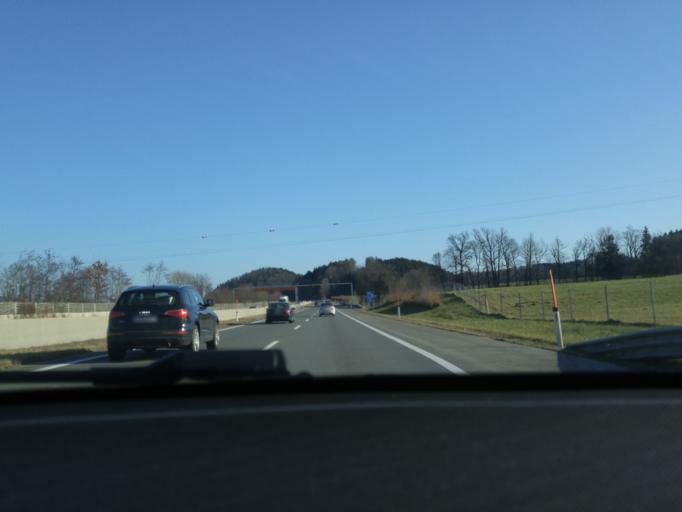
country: AT
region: Salzburg
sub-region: Politischer Bezirk Salzburg-Umgebung
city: Plainfeld
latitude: 47.8517
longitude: 13.1724
